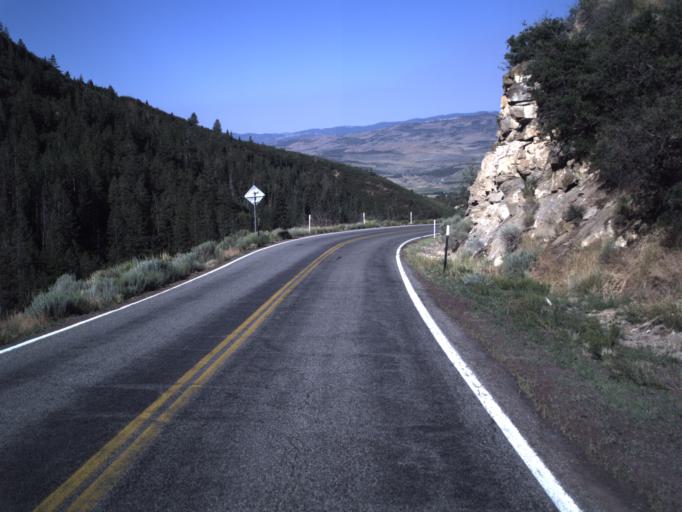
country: US
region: Utah
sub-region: Sanpete County
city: Fairview
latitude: 39.6491
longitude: -111.3903
